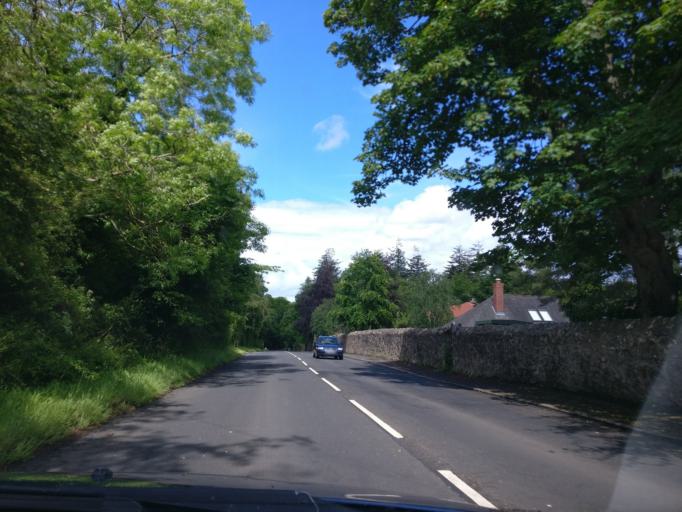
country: GB
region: Scotland
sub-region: East Lothian
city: Haddington
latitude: 55.9000
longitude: -2.7519
